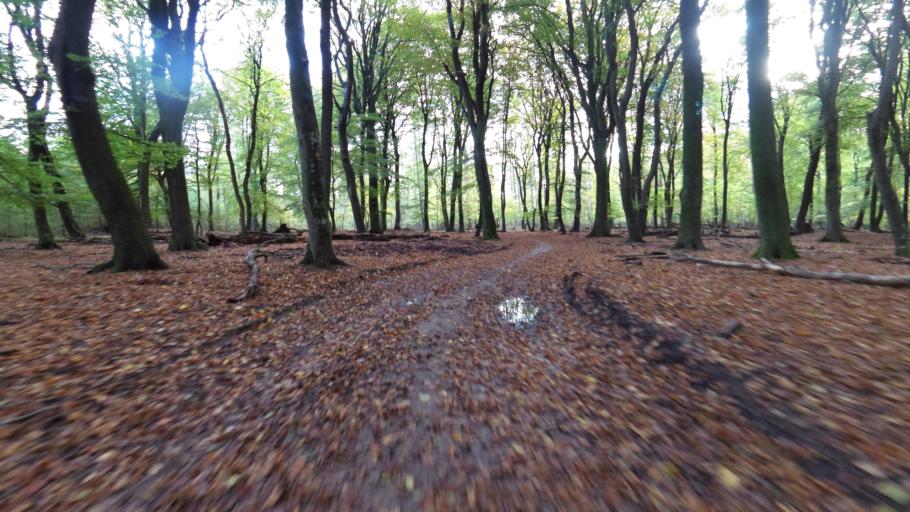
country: NL
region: Gelderland
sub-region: Gemeente Nunspeet
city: Nunspeet
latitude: 52.3204
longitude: 5.8314
